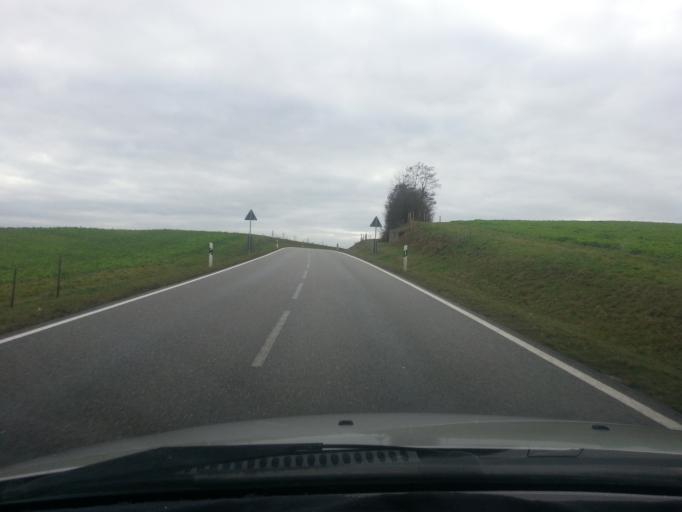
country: DE
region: Baden-Wuerttemberg
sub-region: Regierungsbezirk Stuttgart
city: Ittlingen
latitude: 49.1672
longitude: 8.9349
